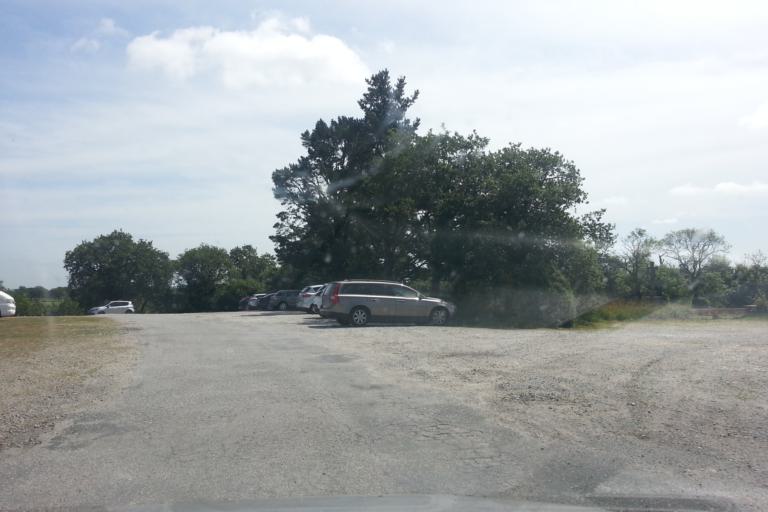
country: FR
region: Brittany
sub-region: Departement du Morbihan
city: Le Faouet
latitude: 48.0421
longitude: -3.4815
